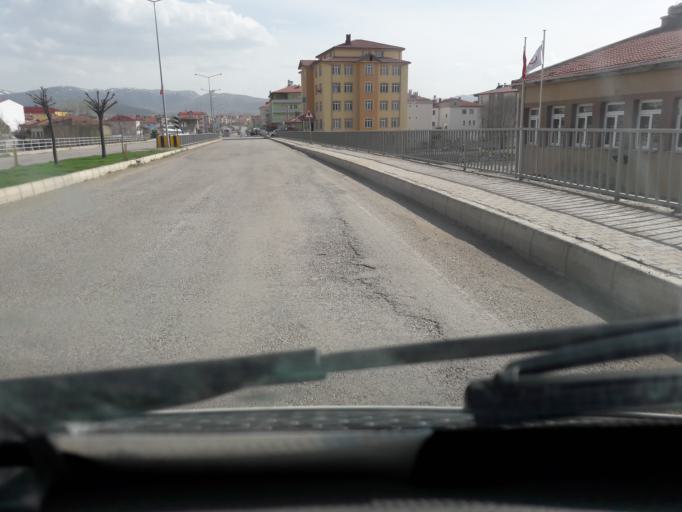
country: TR
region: Gumushane
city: Kelkit
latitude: 40.1375
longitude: 39.4333
